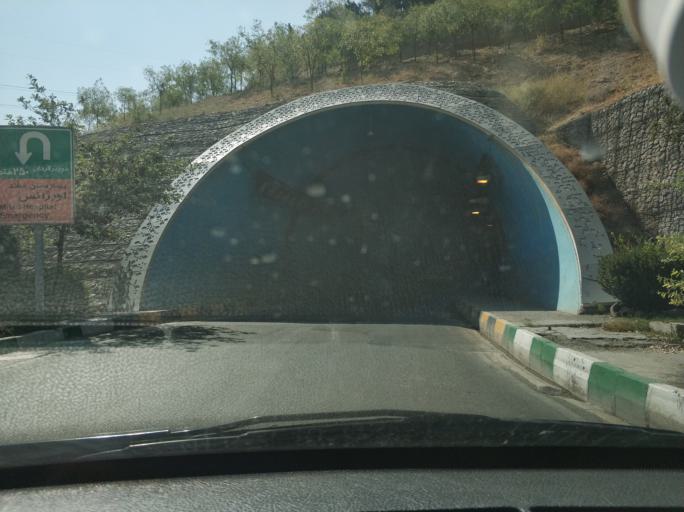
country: IR
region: Tehran
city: Tehran
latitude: 35.7442
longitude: 51.3800
